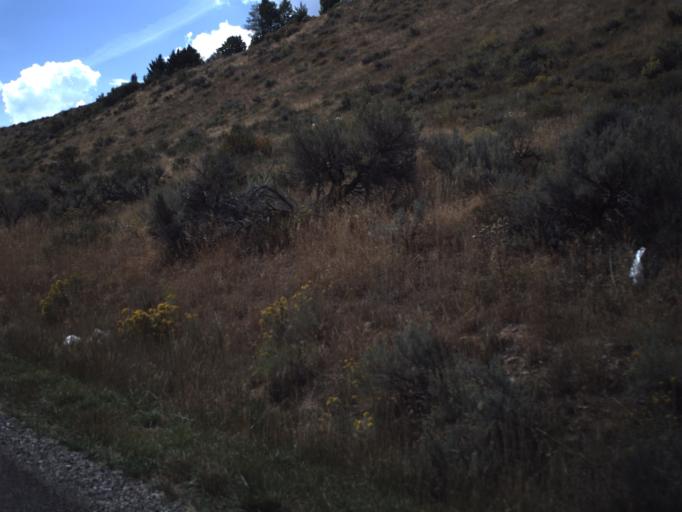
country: US
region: Utah
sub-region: Rich County
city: Randolph
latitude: 41.8932
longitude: -111.3665
